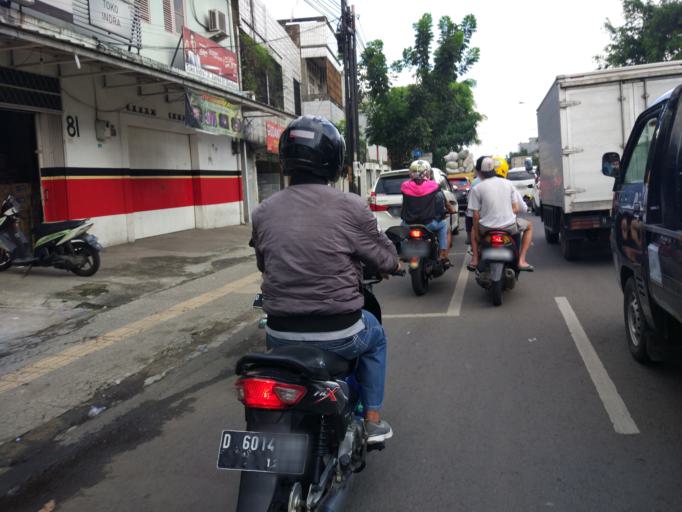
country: ID
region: West Java
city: Bandung
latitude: -6.9229
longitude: 107.5858
